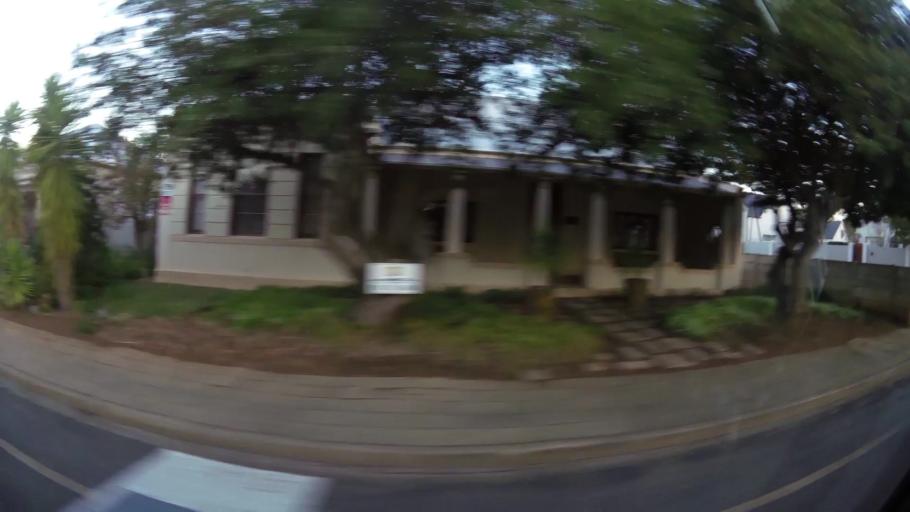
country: ZA
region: Western Cape
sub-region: Eden District Municipality
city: Riversdale
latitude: -34.0903
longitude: 21.2575
